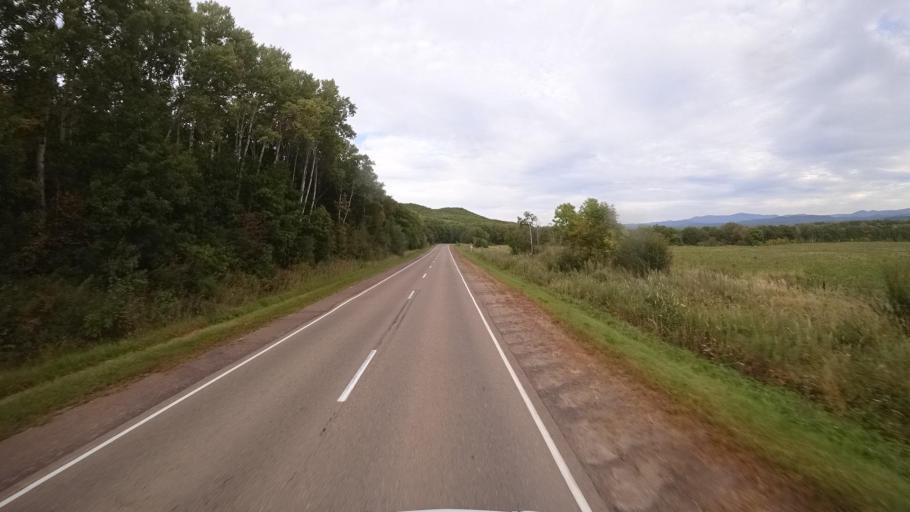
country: RU
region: Primorskiy
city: Yakovlevka
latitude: 44.3765
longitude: 133.4439
